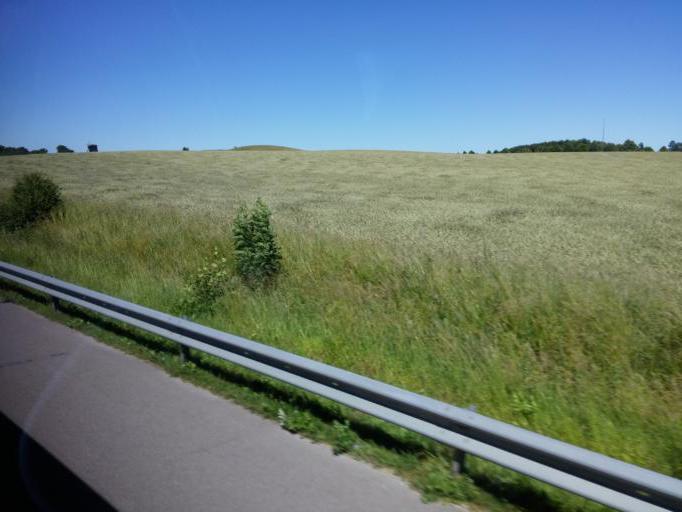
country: SE
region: Skane
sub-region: Malmo
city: Oxie
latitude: 55.5402
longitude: 13.1639
